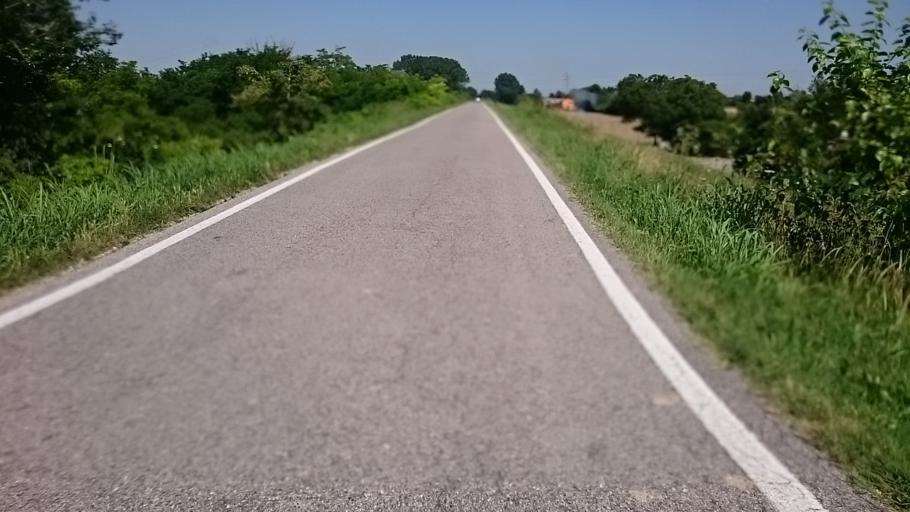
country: IT
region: Veneto
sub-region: Provincia di Venezia
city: Galta
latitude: 45.3788
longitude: 12.0236
